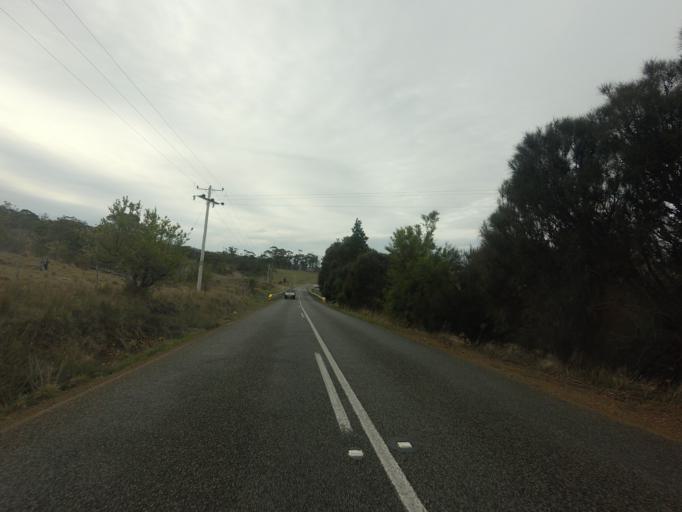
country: AU
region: Tasmania
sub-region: Sorell
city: Sorell
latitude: -42.2172
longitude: 148.0305
